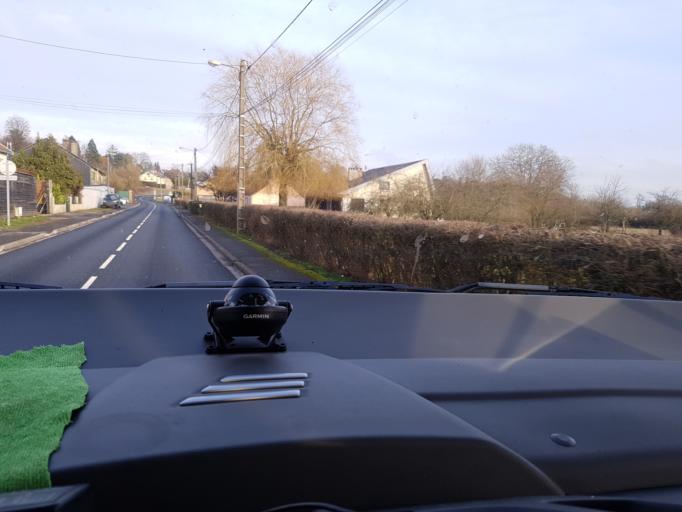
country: FR
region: Champagne-Ardenne
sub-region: Departement des Ardennes
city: Warcq
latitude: 49.7768
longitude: 4.6868
